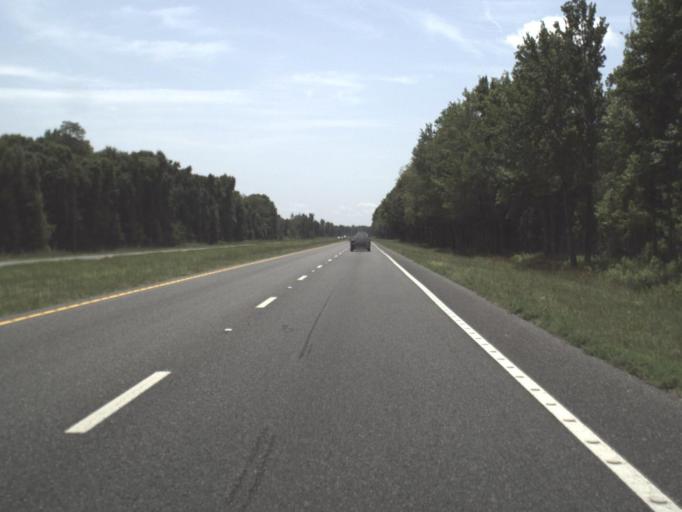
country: US
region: Florida
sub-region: Taylor County
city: Perry
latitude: 29.9565
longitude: -83.4640
